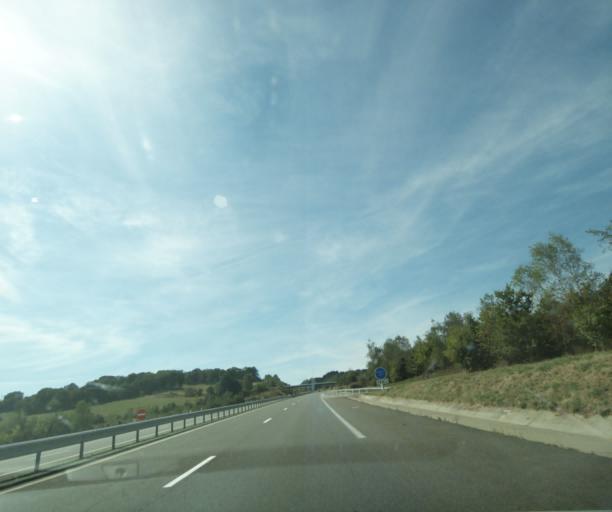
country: FR
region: Auvergne
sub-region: Departement du Puy-de-Dome
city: Chapdes-Beaufort
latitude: 45.8344
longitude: 2.8187
